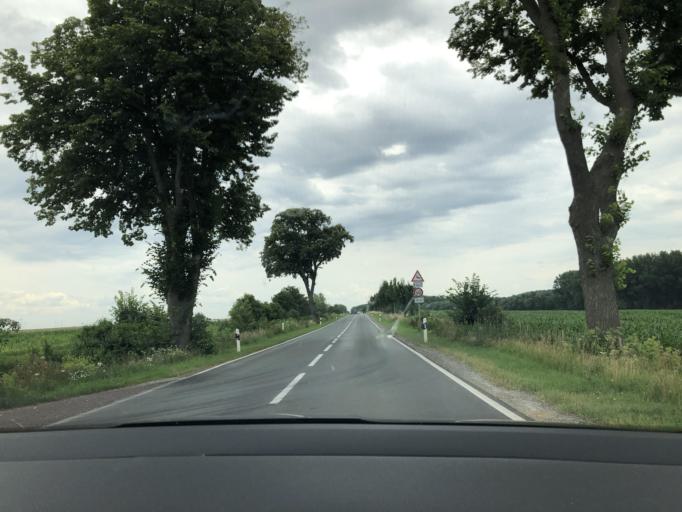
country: DE
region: Saxony-Anhalt
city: Wolmirsleben
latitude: 51.9427
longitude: 11.5015
